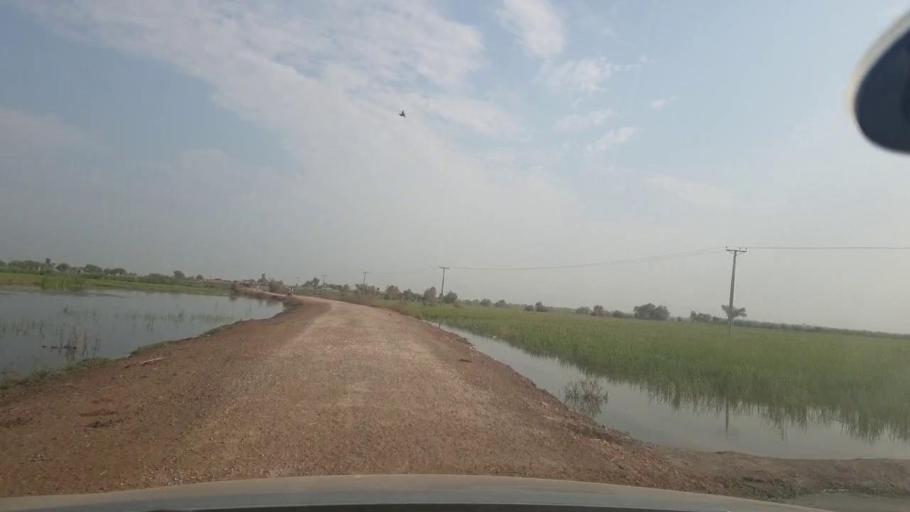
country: PK
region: Balochistan
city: Mehrabpur
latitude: 28.0691
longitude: 68.2108
